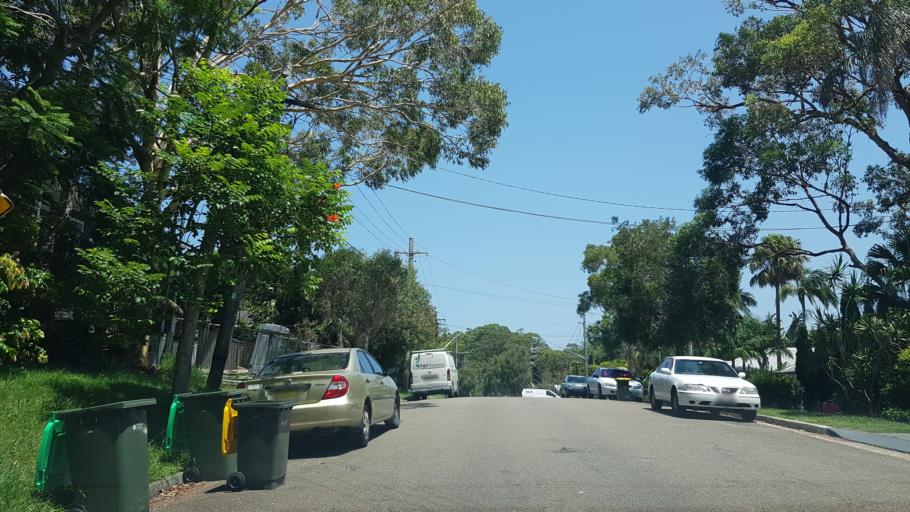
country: AU
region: New South Wales
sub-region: Pittwater
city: Newport
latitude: -33.6558
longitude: 151.3115
